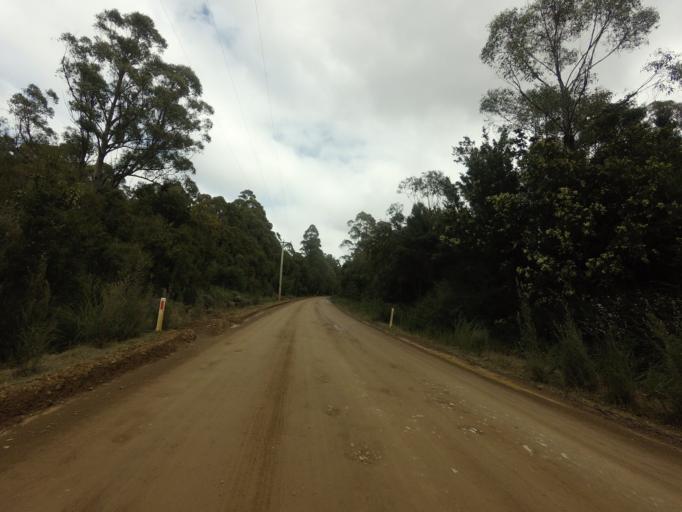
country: AU
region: Tasmania
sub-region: Huon Valley
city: Geeveston
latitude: -43.4138
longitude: 146.8943
